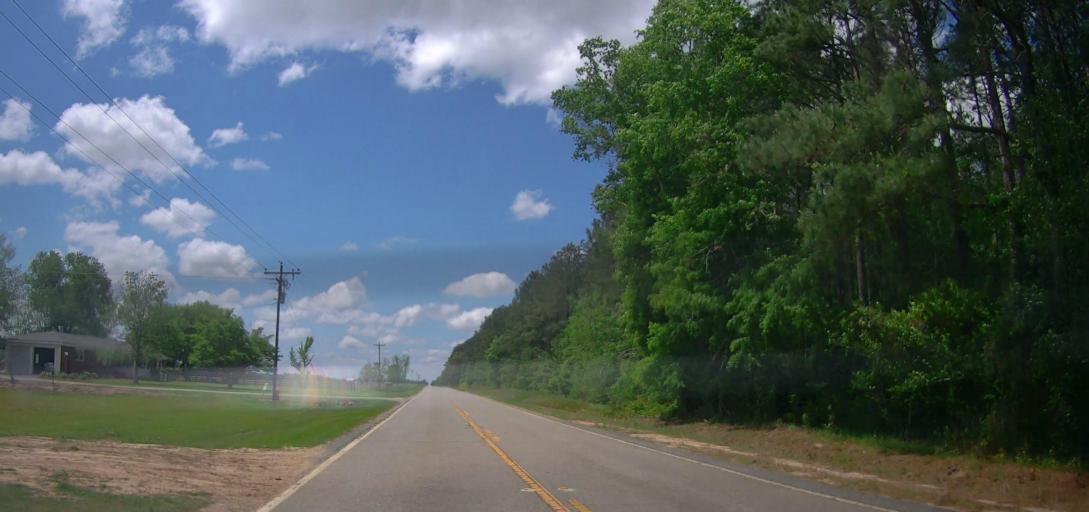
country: US
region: Georgia
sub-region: Dodge County
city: Chester
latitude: 32.5003
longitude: -83.2406
